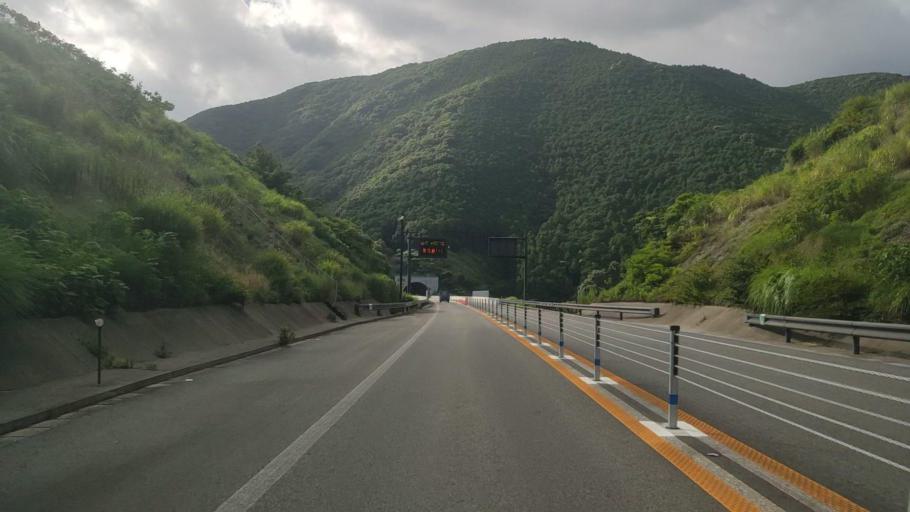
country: JP
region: Wakayama
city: Tanabe
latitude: 33.5598
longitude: 135.5060
